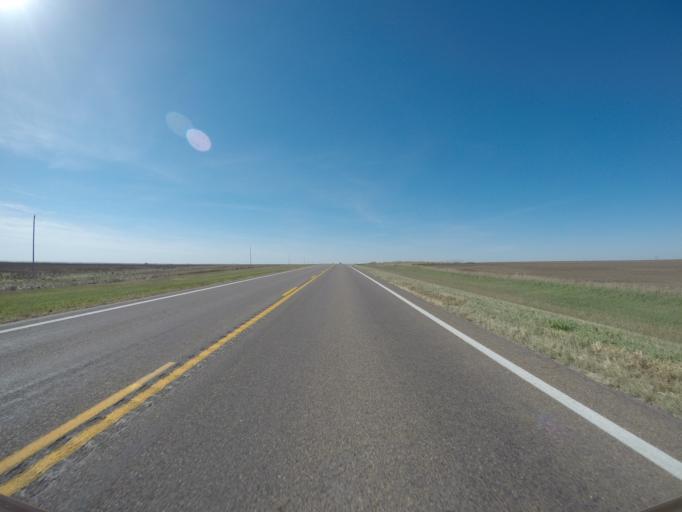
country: US
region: Kansas
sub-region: Smith County
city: Smith Center
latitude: 39.7710
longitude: -98.9464
